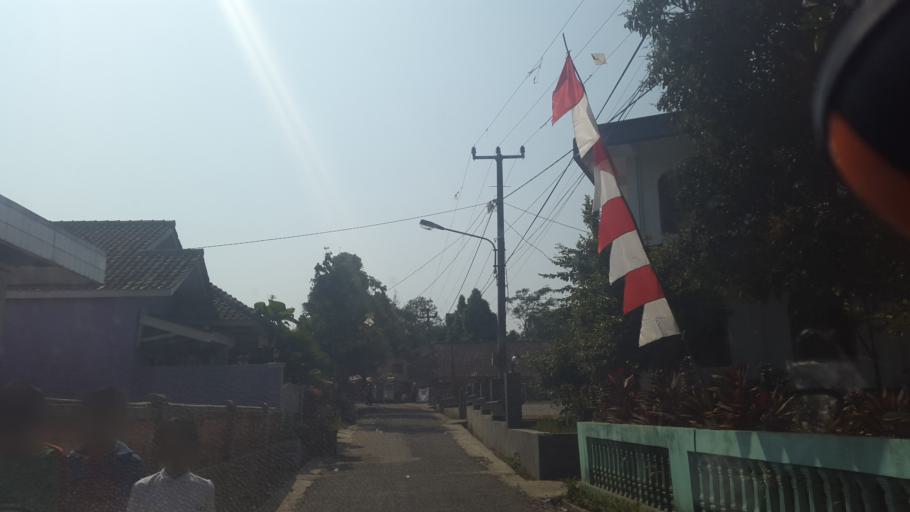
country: ID
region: West Java
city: Sukabumi
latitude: -6.8858
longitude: 106.8476
